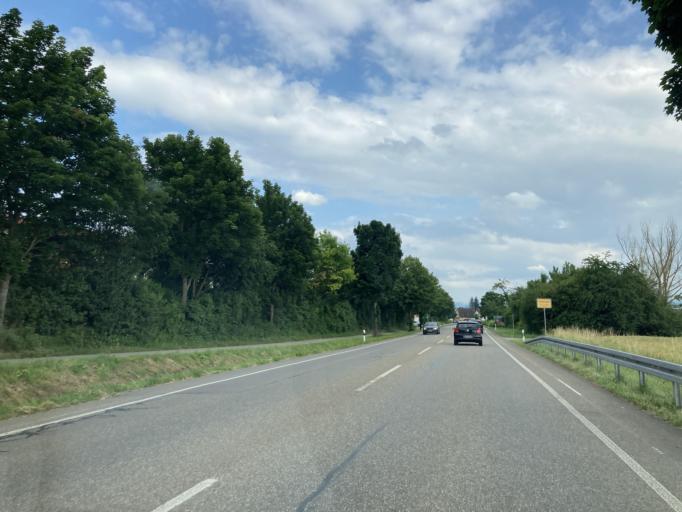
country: DE
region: Baden-Wuerttemberg
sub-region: Freiburg Region
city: Teningen
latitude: 48.1413
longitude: 7.7994
